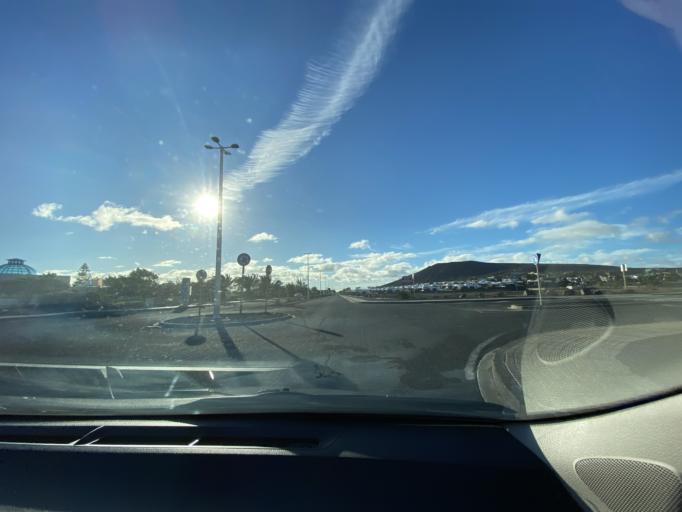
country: ES
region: Canary Islands
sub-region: Provincia de Las Palmas
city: Playa Blanca
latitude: 28.8666
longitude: -13.8379
